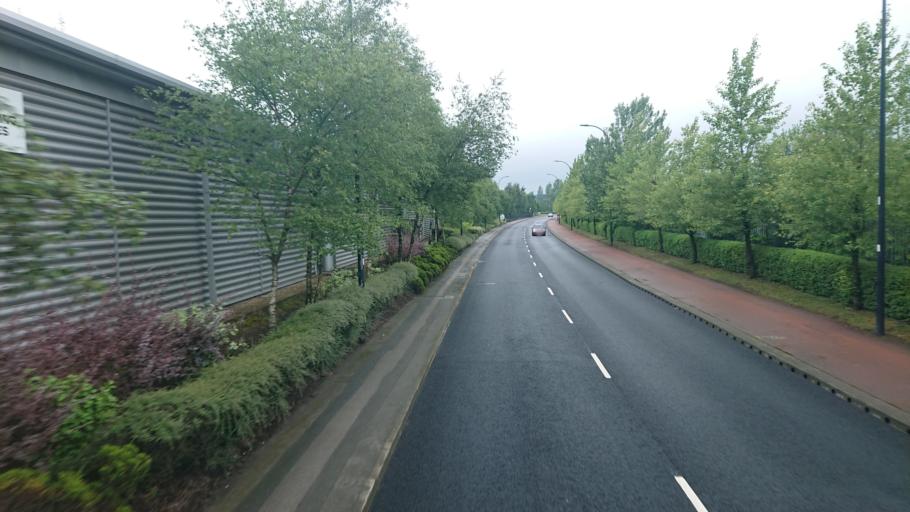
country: GB
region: England
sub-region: Rotherham
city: Orgreave
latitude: 53.3959
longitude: -1.3949
